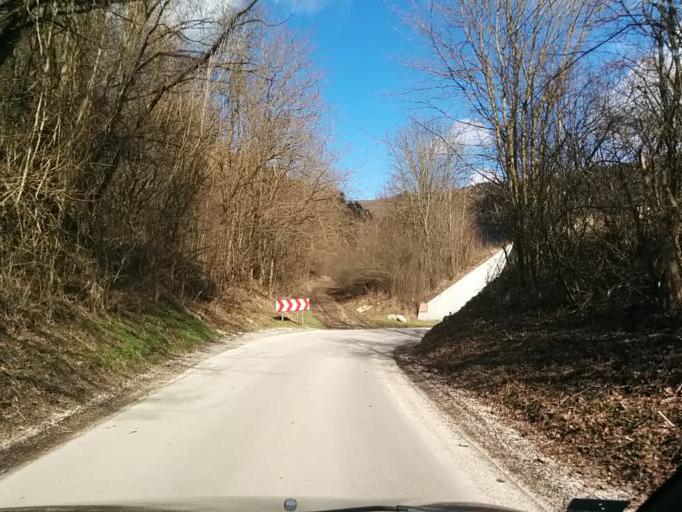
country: SK
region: Nitriansky
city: Cachtice
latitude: 48.7292
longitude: 17.7751
